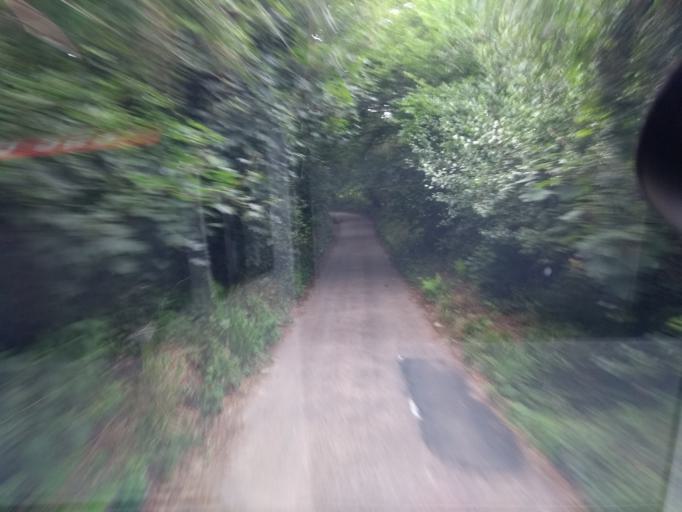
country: GB
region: England
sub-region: Dorset
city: Bridport
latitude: 50.7303
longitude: -2.7954
